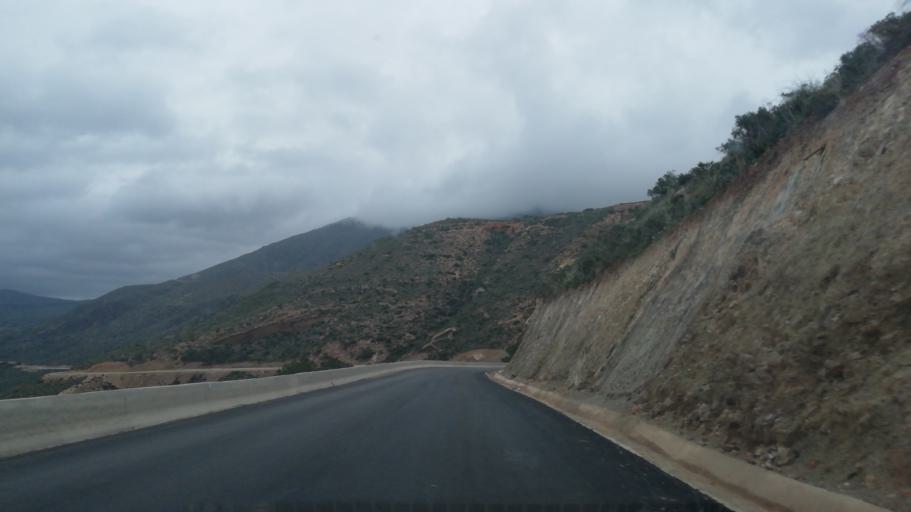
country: DZ
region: Oran
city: Bir el Djir
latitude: 35.7647
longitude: -0.5263
